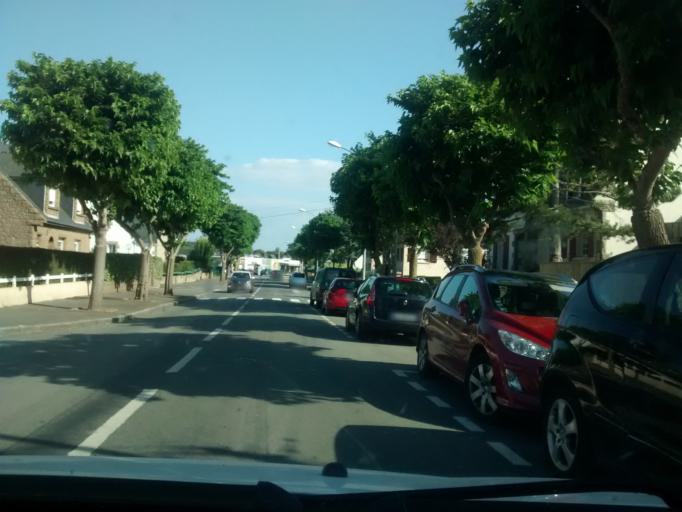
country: FR
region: Brittany
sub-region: Departement d'Ille-et-Vilaine
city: Saint-Malo
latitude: 48.6695
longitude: -1.9813
